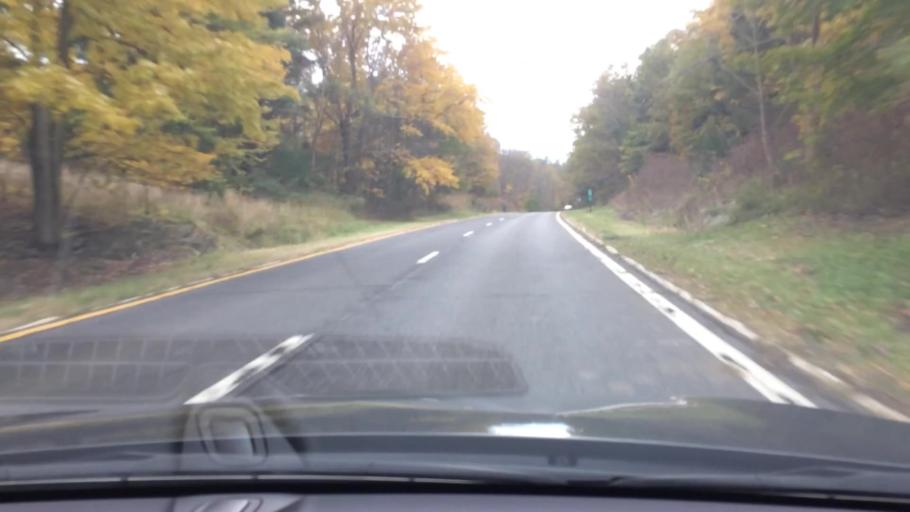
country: US
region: New York
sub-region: Dutchess County
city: Pleasant Valley
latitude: 41.7414
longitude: -73.7738
